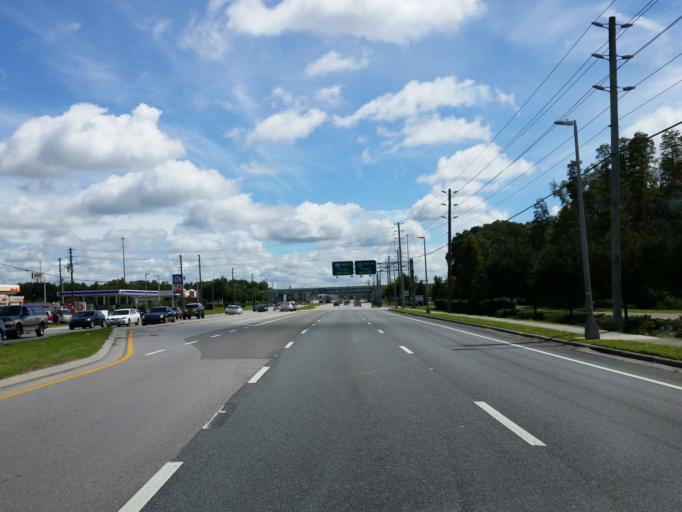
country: US
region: Florida
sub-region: Pasco County
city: Wesley Chapel
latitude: 28.2376
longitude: -82.3590
